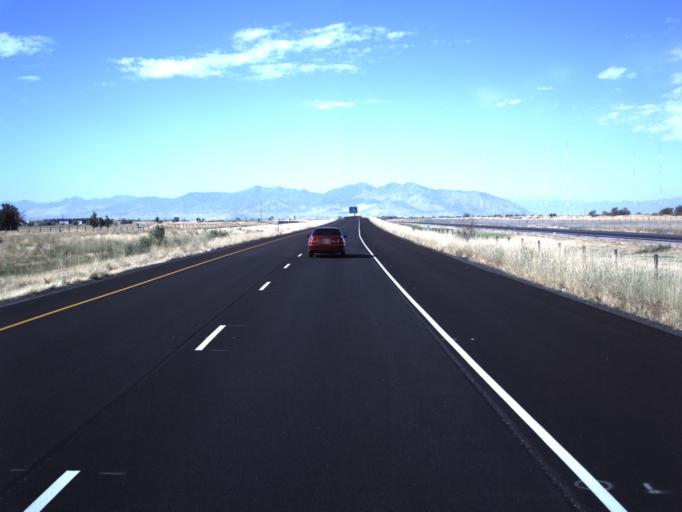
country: US
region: Utah
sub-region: Davis County
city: West Bountiful
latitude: 40.8981
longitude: -111.9293
